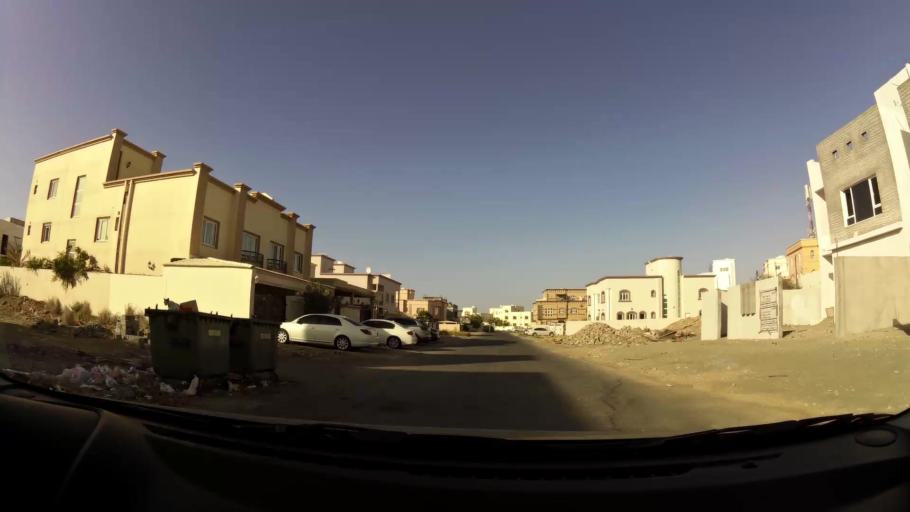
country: OM
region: Muhafazat Masqat
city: As Sib al Jadidah
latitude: 23.6022
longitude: 58.2137
